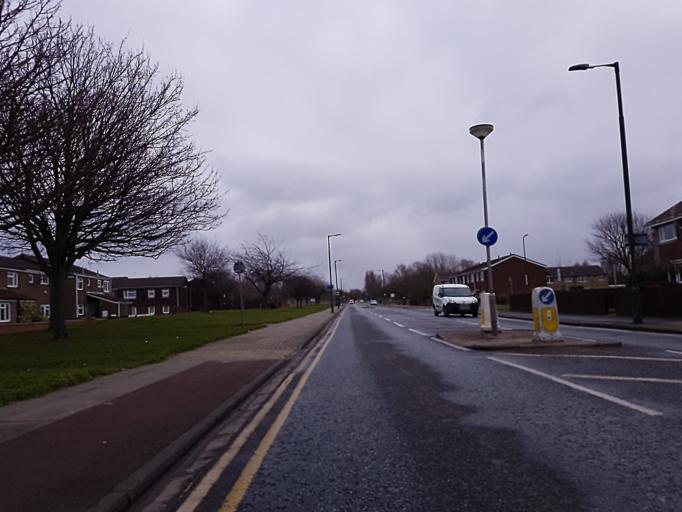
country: GB
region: England
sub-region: North East Lincolnshire
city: Great Coates
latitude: 53.5707
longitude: -0.1204
